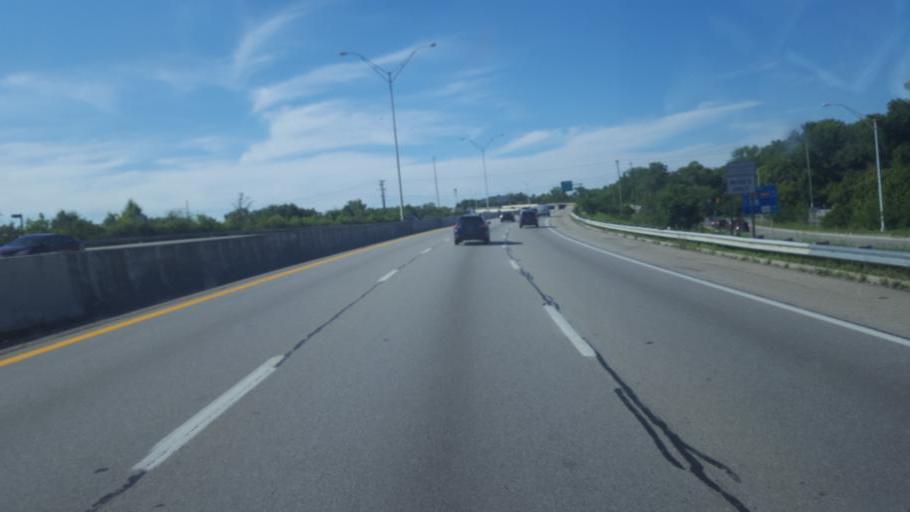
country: US
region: Ohio
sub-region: Franklin County
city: Bexley
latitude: 39.9468
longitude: -82.9434
